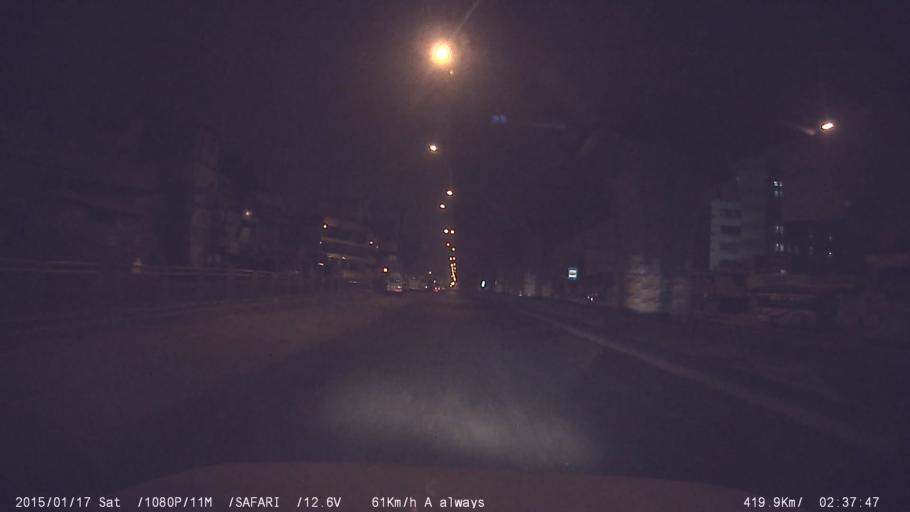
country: IN
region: Karnataka
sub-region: Bangalore Urban
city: Bangalore
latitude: 12.9062
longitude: 77.6293
